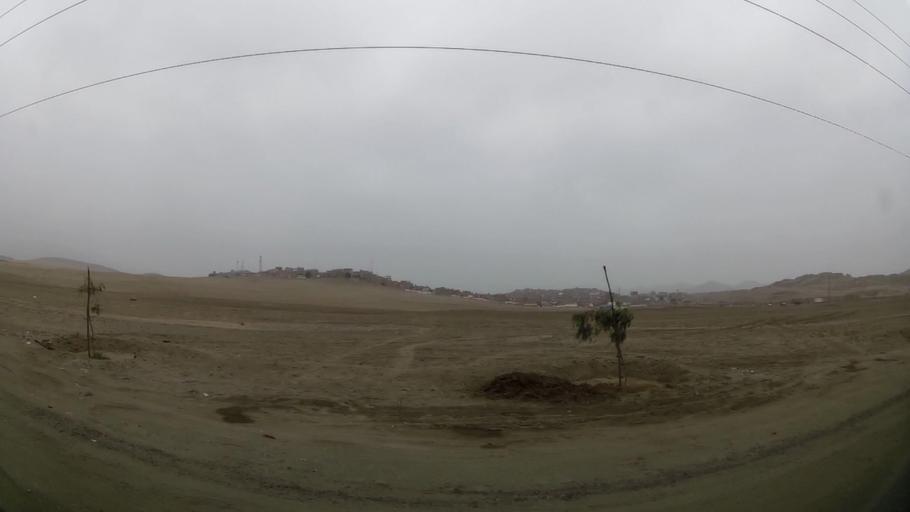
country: PE
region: Lima
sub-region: Lima
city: Punta Hermosa
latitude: -12.2521
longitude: -76.9052
